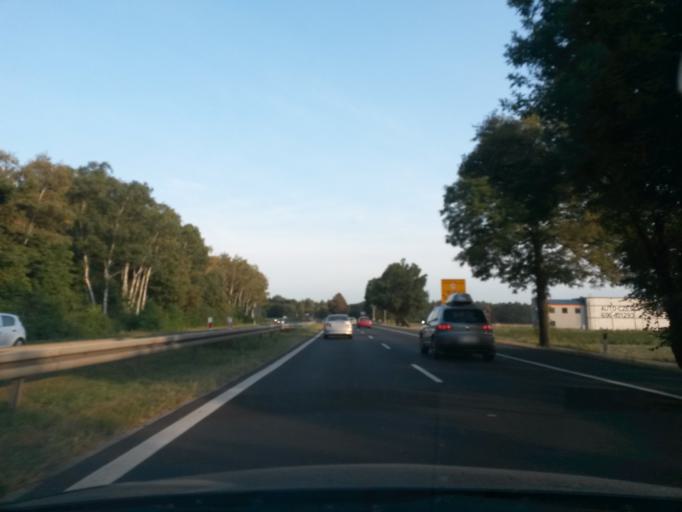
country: PL
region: Masovian Voivodeship
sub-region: Powiat nowodworski
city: Zakroczym
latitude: 52.4568
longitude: 20.5794
